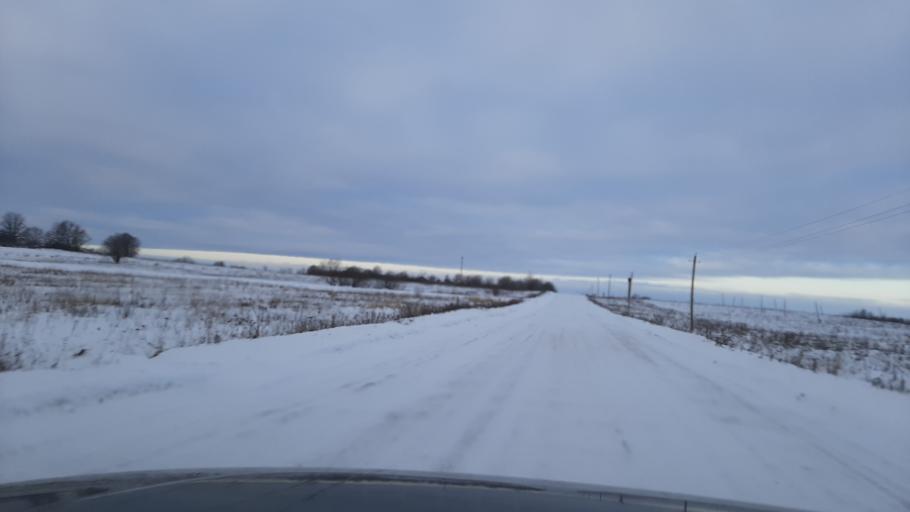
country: RU
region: Kostroma
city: Kosmynino
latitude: 57.4461
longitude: 40.9234
